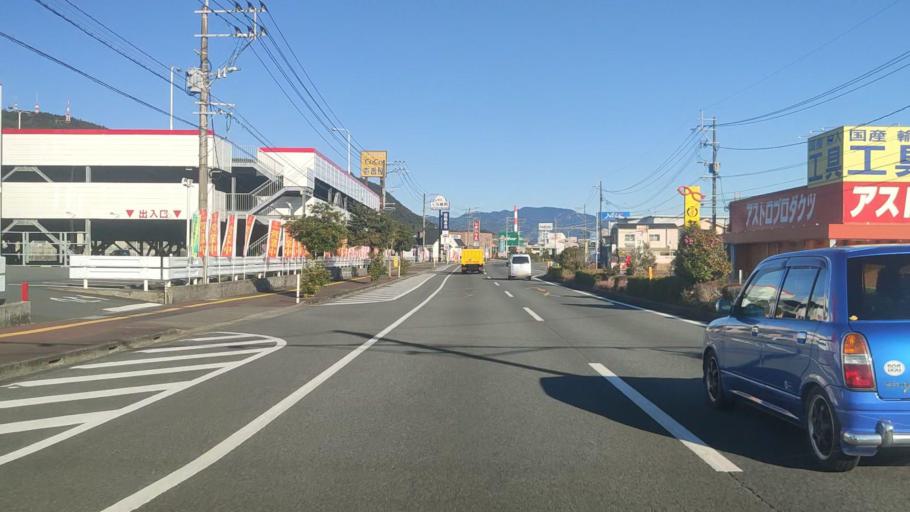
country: JP
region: Miyazaki
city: Nobeoka
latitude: 32.5467
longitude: 131.6775
